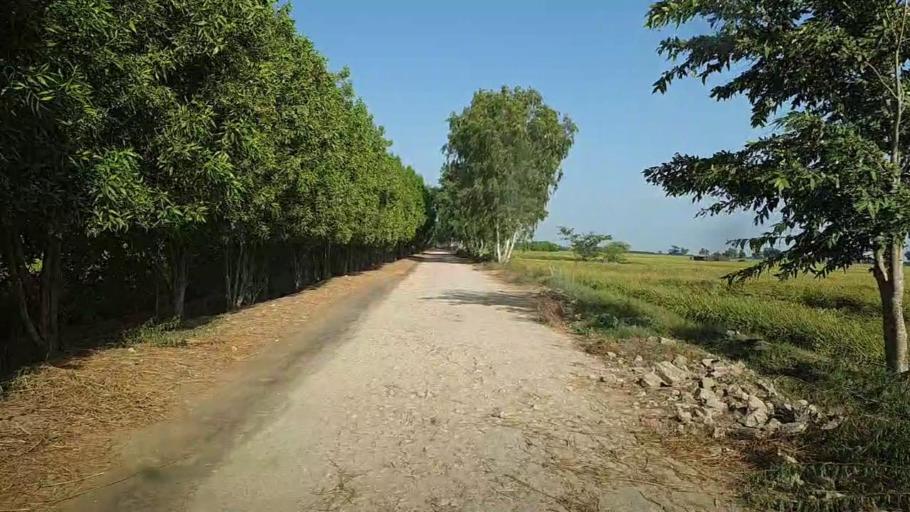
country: PK
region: Sindh
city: Kario
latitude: 24.5997
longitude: 68.5099
